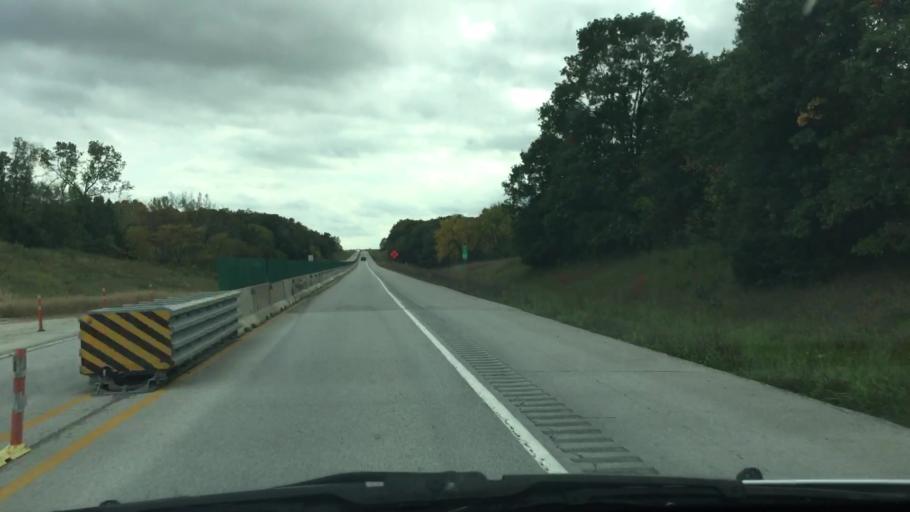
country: US
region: Iowa
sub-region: Decatur County
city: Leon
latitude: 40.6989
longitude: -93.8461
